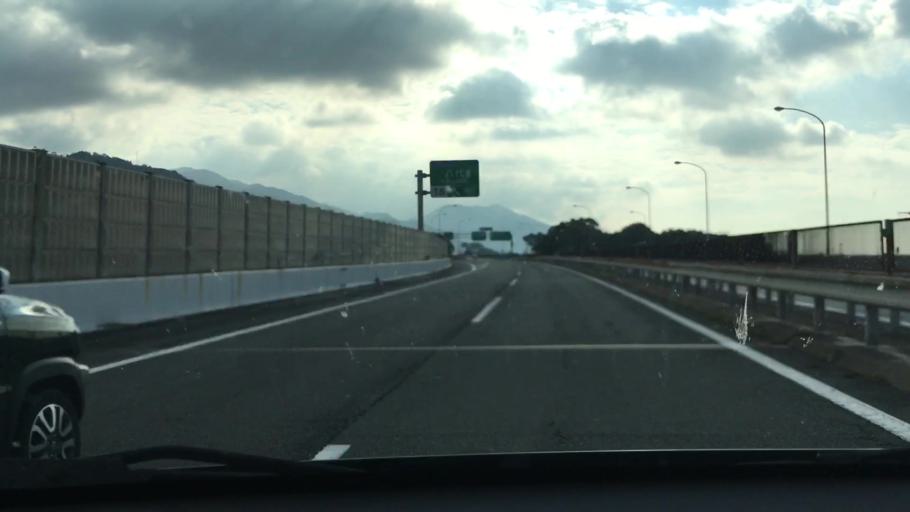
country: JP
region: Kumamoto
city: Yatsushiro
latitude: 32.5159
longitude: 130.6496
